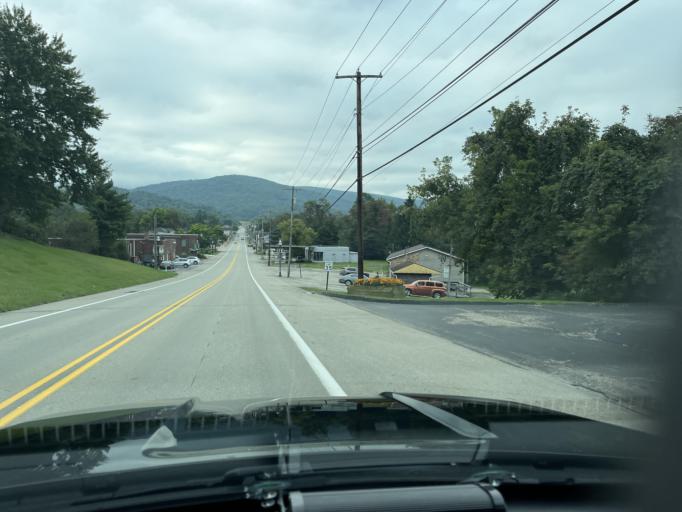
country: US
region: Pennsylvania
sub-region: Fayette County
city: Hopwood
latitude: 39.8798
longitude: -79.7037
